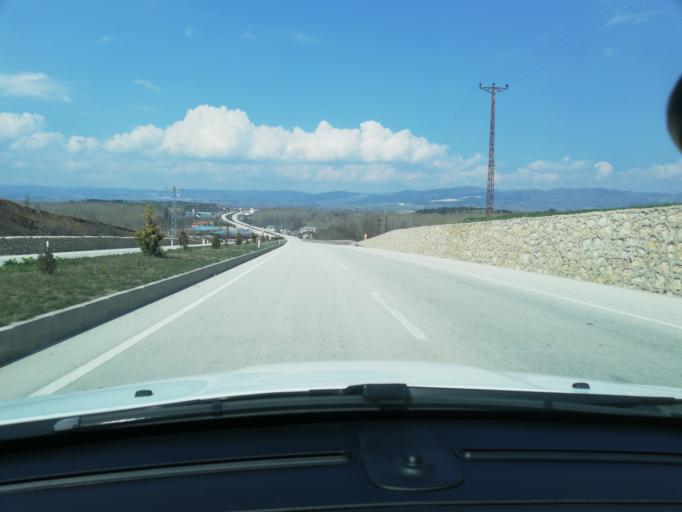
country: TR
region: Kastamonu
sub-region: Cide
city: Kastamonu
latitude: 41.4377
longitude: 33.7980
